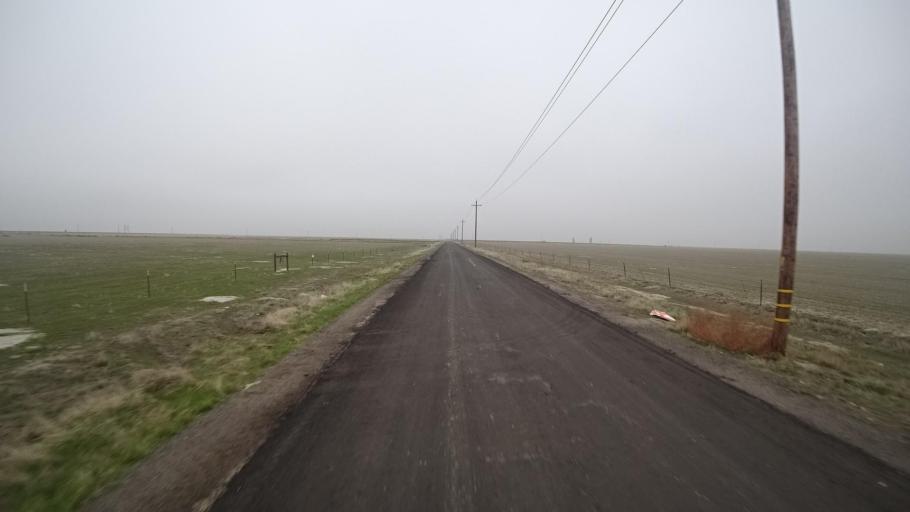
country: US
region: California
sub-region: Tulare County
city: Alpaugh
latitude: 35.7735
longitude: -119.4723
